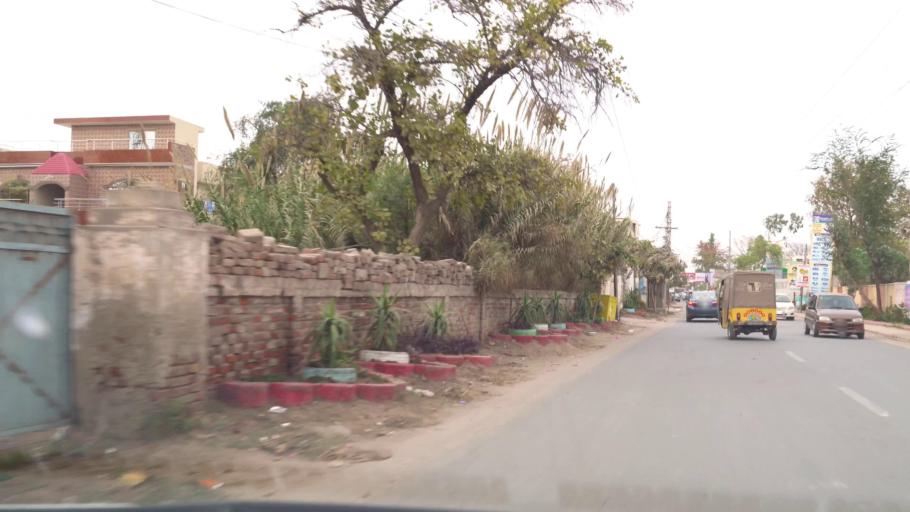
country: PK
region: Punjab
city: Sargodha
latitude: 32.0755
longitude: 72.6785
